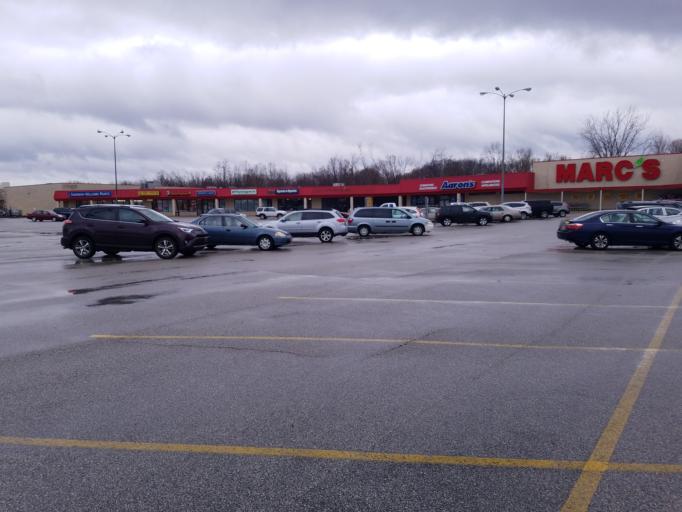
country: US
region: Ohio
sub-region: Lake County
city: North Madison
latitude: 41.8020
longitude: -81.0544
